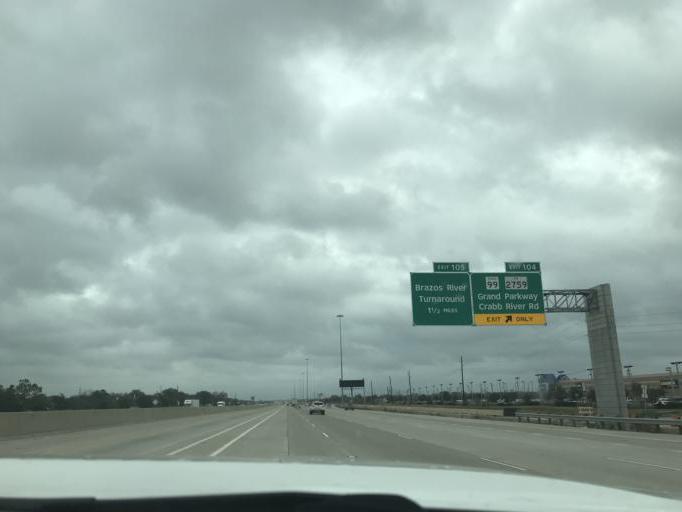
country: US
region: Texas
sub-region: Fort Bend County
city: Greatwood
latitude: 29.5567
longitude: -95.7130
